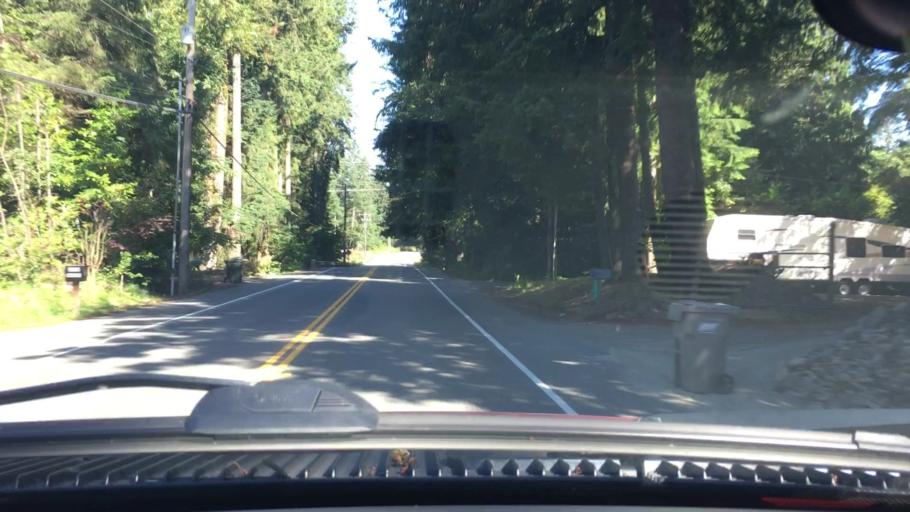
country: US
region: Washington
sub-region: King County
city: Lake Morton-Berrydale
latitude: 47.3299
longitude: -122.1184
